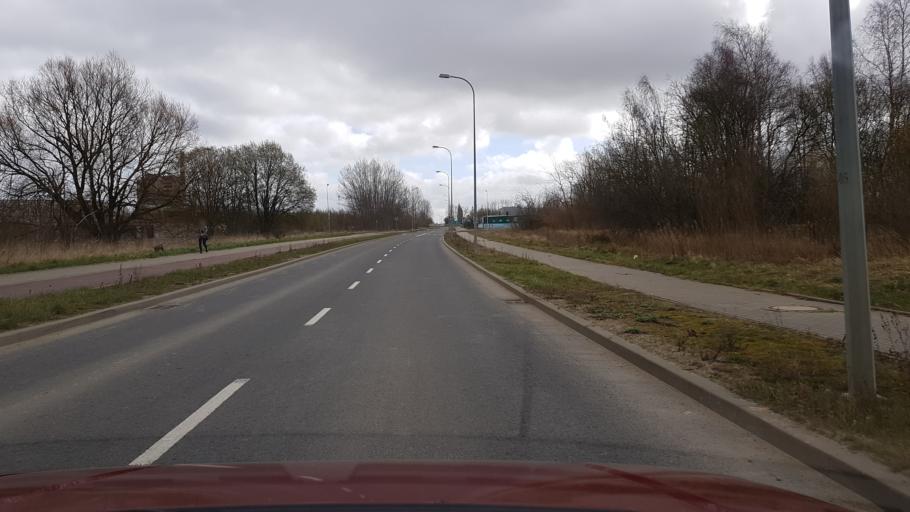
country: PL
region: West Pomeranian Voivodeship
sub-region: Koszalin
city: Koszalin
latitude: 54.1985
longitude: 16.1406
